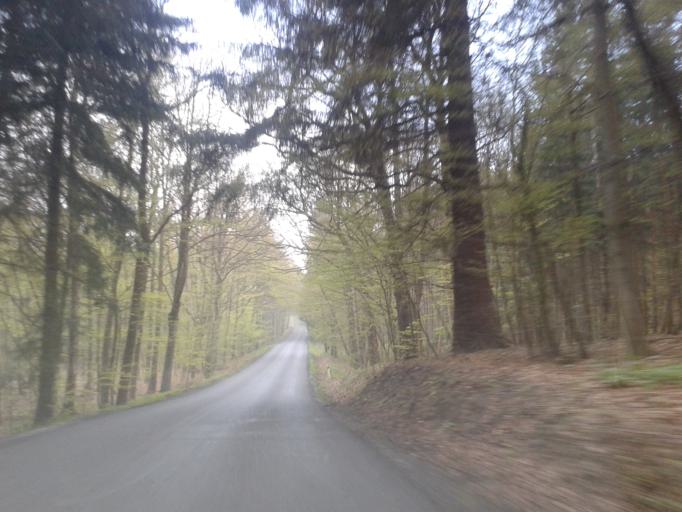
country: CZ
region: Central Bohemia
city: Hudlice
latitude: 49.9426
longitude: 13.9082
